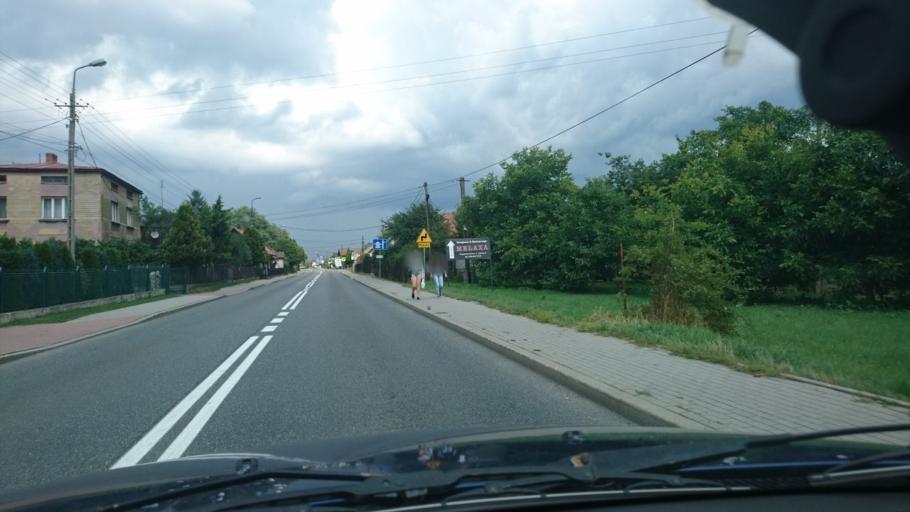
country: PL
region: Silesian Voivodeship
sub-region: Powiat zywiecki
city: Cisiec
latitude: 49.5989
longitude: 19.1086
